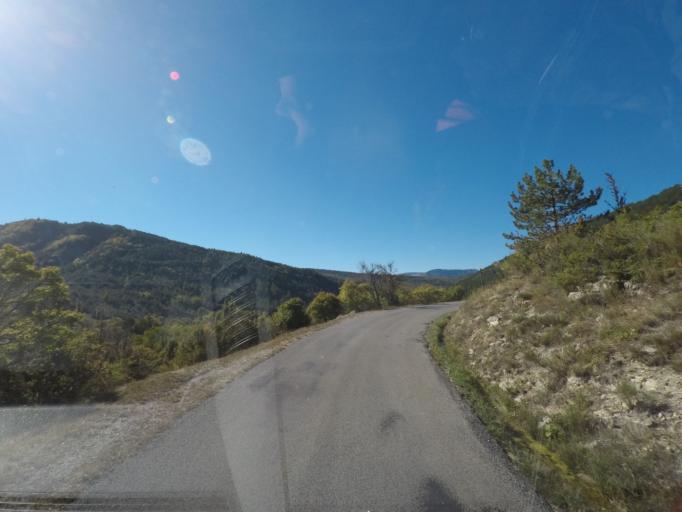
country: FR
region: Rhone-Alpes
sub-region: Departement de la Drome
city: Die
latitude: 44.5556
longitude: 5.3522
